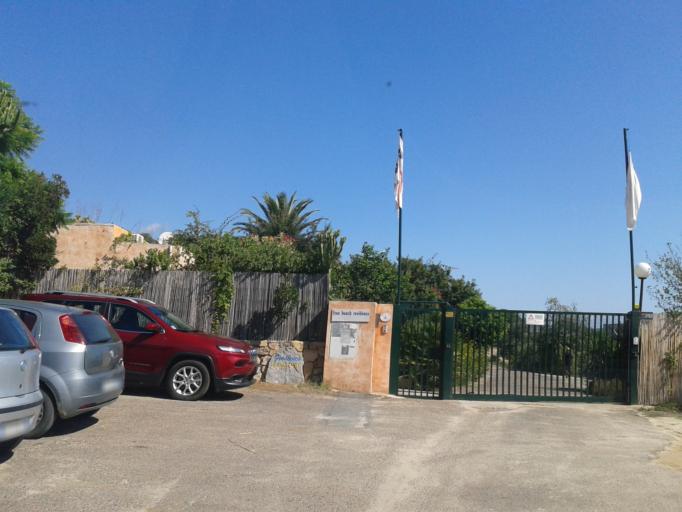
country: IT
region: Sardinia
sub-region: Provincia di Cagliari
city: Olia Speciosa
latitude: 39.2529
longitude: 9.5744
